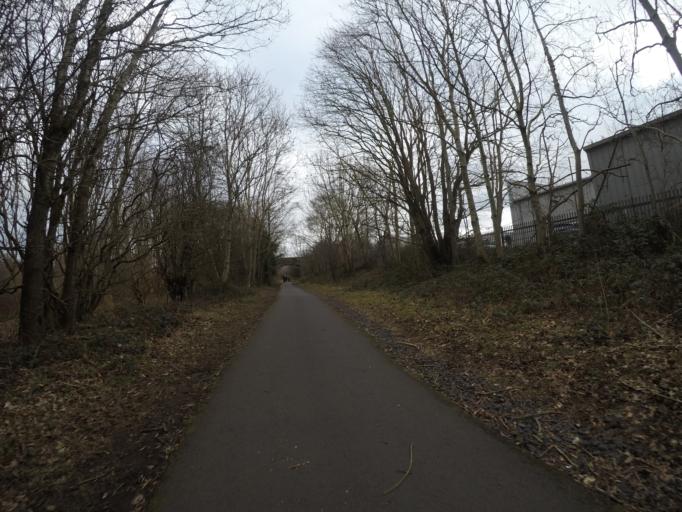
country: GB
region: Scotland
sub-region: North Ayrshire
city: Dreghorn
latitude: 55.6088
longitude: -4.6360
